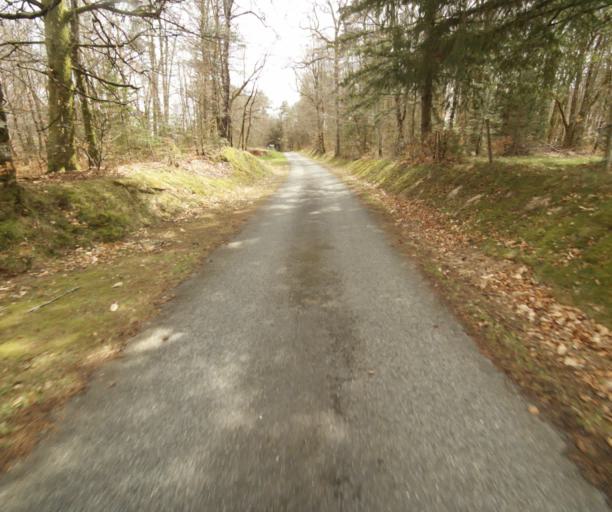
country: FR
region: Limousin
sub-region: Departement de la Correze
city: Laguenne
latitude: 45.2187
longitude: 1.8992
